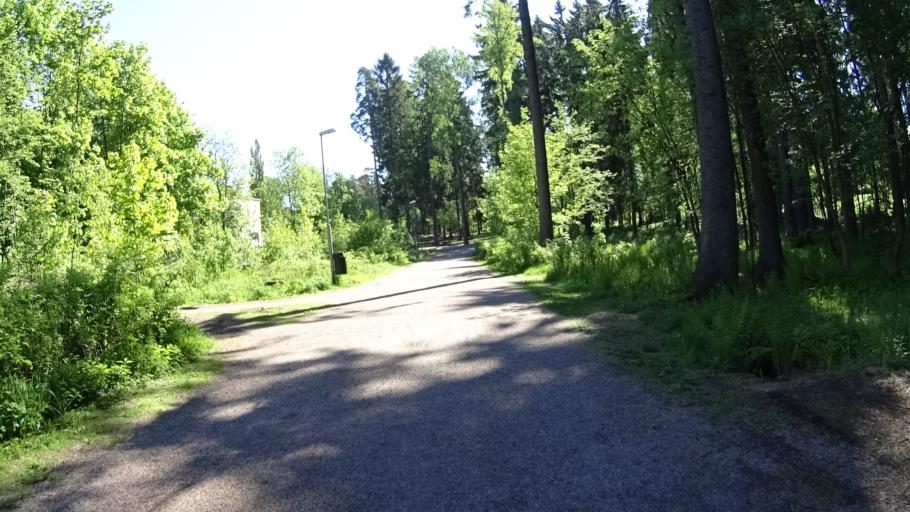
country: FI
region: Uusimaa
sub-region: Helsinki
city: Teekkarikylae
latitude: 60.2070
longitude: 24.8678
